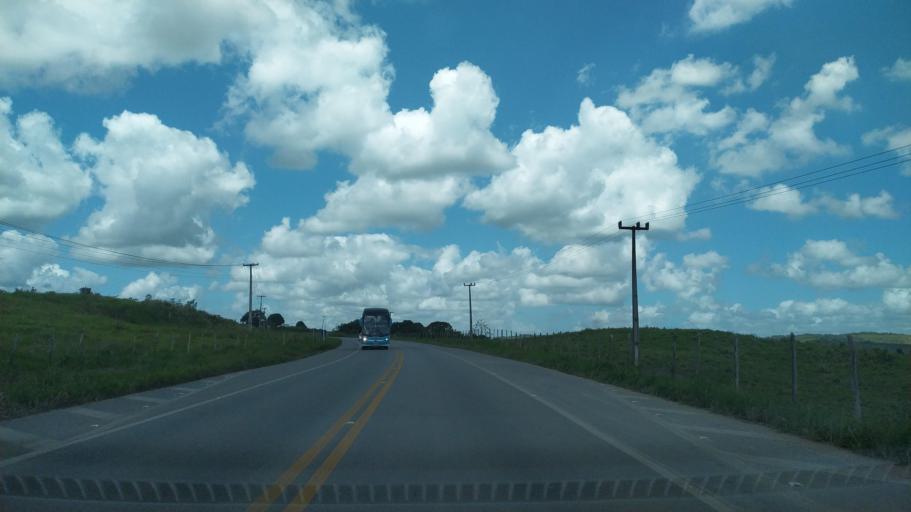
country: BR
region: Alagoas
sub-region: Murici
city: Murici
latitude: -9.2990
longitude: -35.9573
